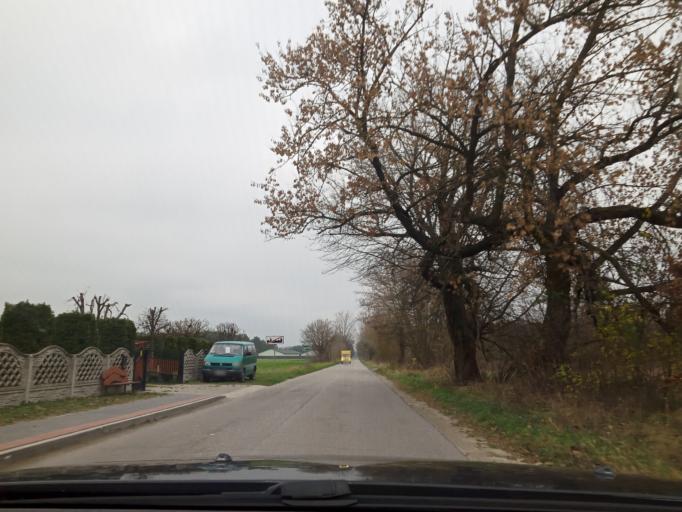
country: PL
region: Swietokrzyskie
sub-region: Powiat jedrzejowski
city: Imielno
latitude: 50.5853
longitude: 20.4549
